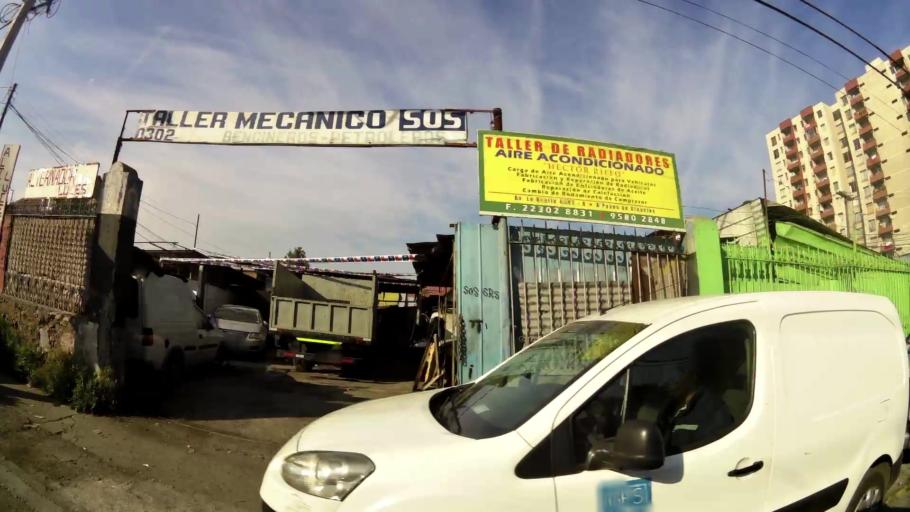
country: CL
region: Santiago Metropolitan
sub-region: Provincia de Santiago
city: Santiago
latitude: -33.5136
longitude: -70.6620
